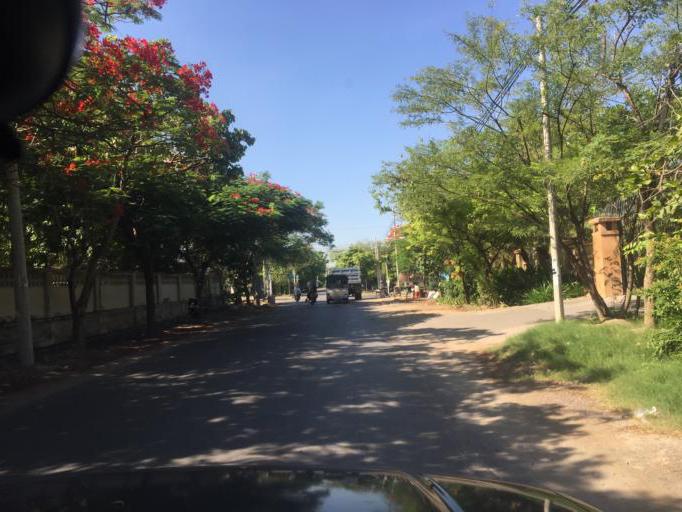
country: MM
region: Mandalay
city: Mandalay
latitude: 21.9520
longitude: 96.1097
